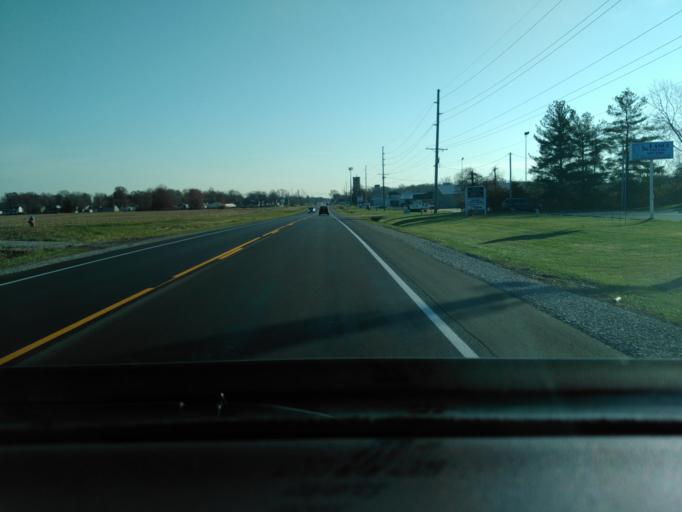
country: US
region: Illinois
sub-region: Madison County
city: Troy
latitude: 38.7176
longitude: -89.8910
